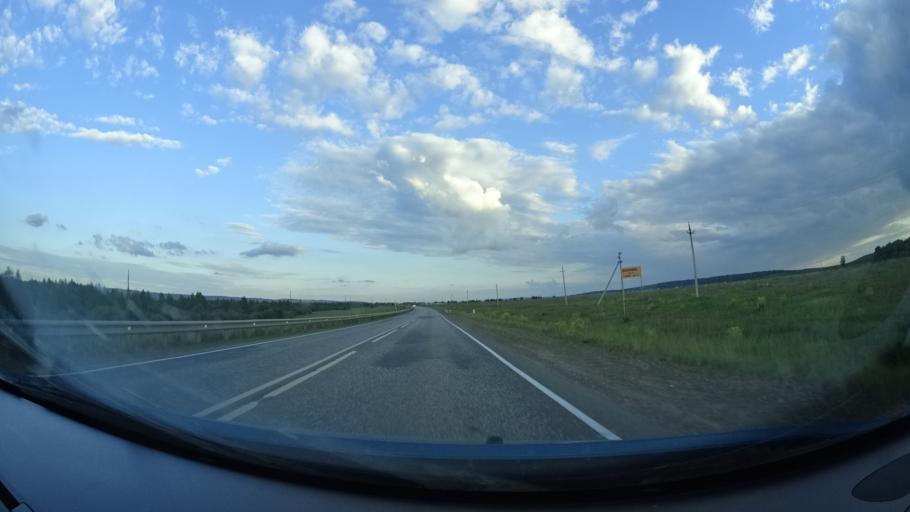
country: RU
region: Perm
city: Barda
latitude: 56.9628
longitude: 55.5792
